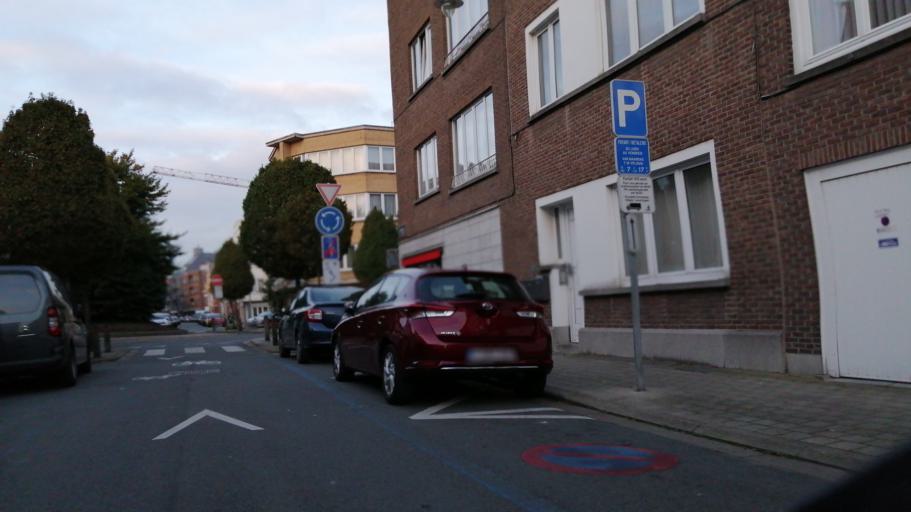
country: BE
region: Flanders
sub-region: Provincie Vlaams-Brabant
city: Bever
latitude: 50.8850
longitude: 4.3349
